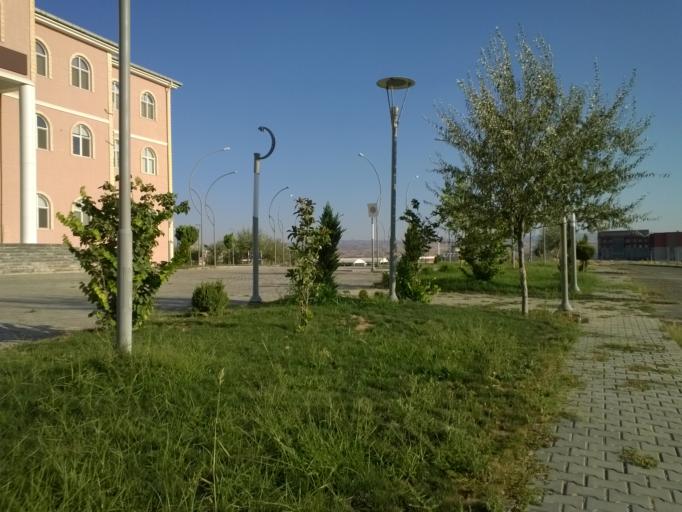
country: TR
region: Batman
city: Oymatas
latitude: 37.7938
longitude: 41.0630
